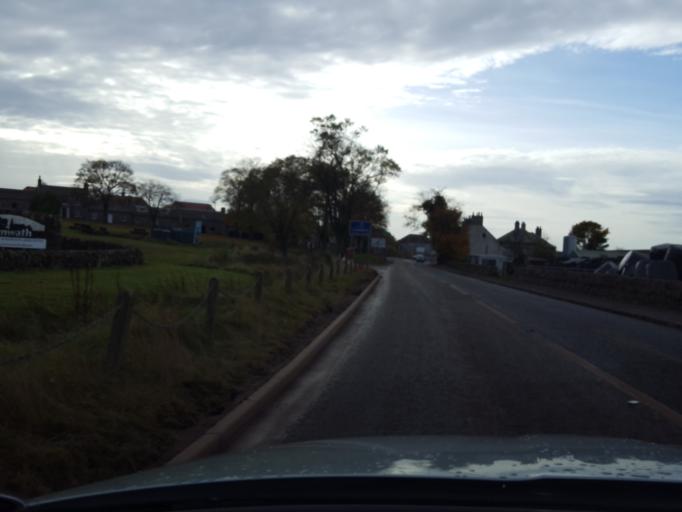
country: GB
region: Scotland
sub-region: South Lanarkshire
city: Carnwath
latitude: 55.7026
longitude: -3.6195
